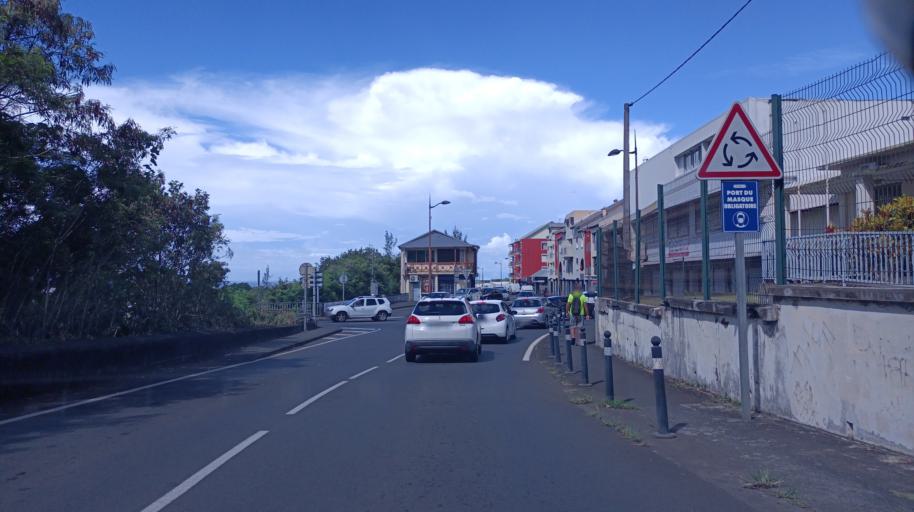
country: RE
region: Reunion
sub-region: Reunion
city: Saint-Joseph
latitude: -21.3762
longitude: 55.6154
